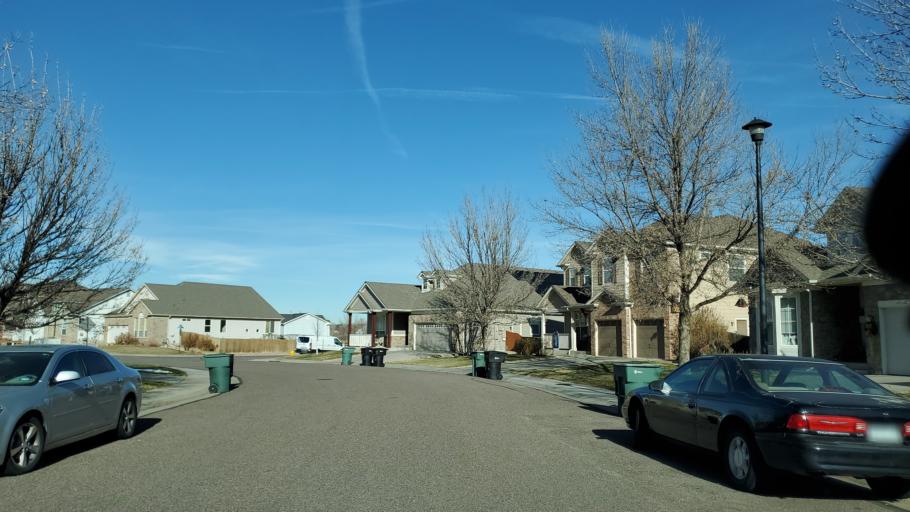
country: US
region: Colorado
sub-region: Adams County
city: Northglenn
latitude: 39.9178
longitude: -104.9457
